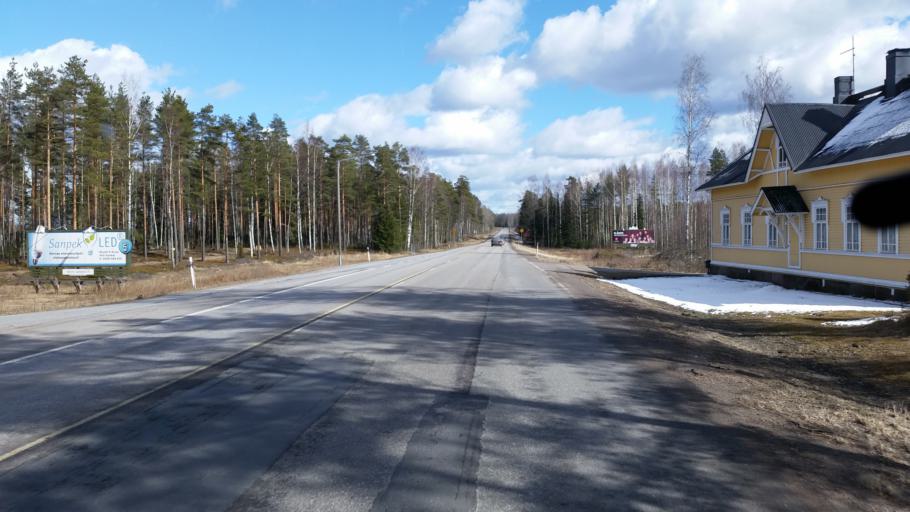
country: FI
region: South Karelia
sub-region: Lappeenranta
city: Lemi
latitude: 60.9604
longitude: 27.8078
